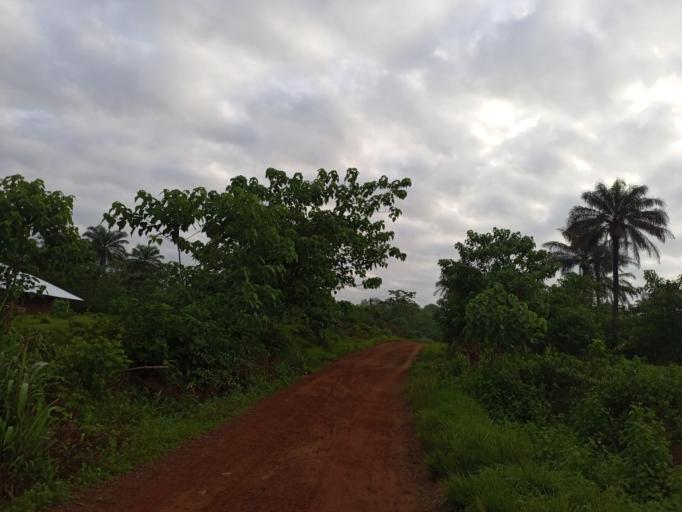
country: SL
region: Eastern Province
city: Pendembu
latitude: 8.1156
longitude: -10.6909
